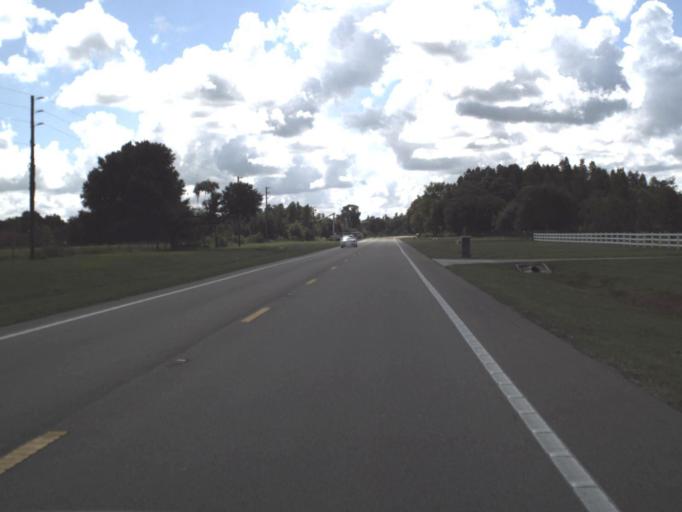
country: US
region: Florida
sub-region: Polk County
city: Kathleen
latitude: 28.2078
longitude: -82.0107
